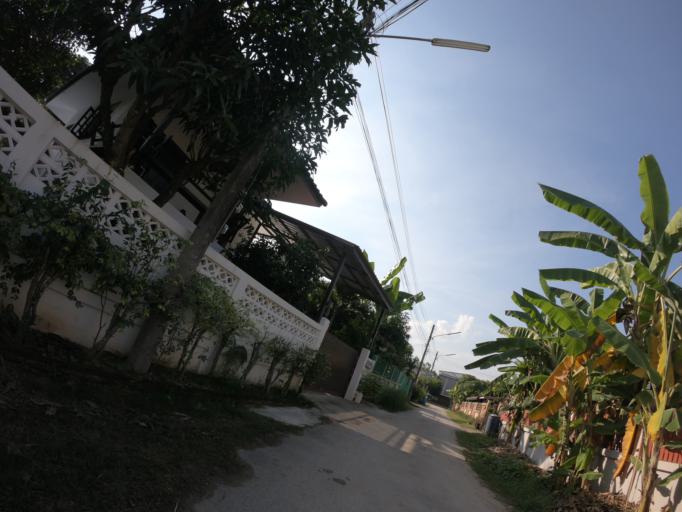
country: TH
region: Chiang Mai
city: Chiang Mai
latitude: 18.8323
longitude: 98.9888
